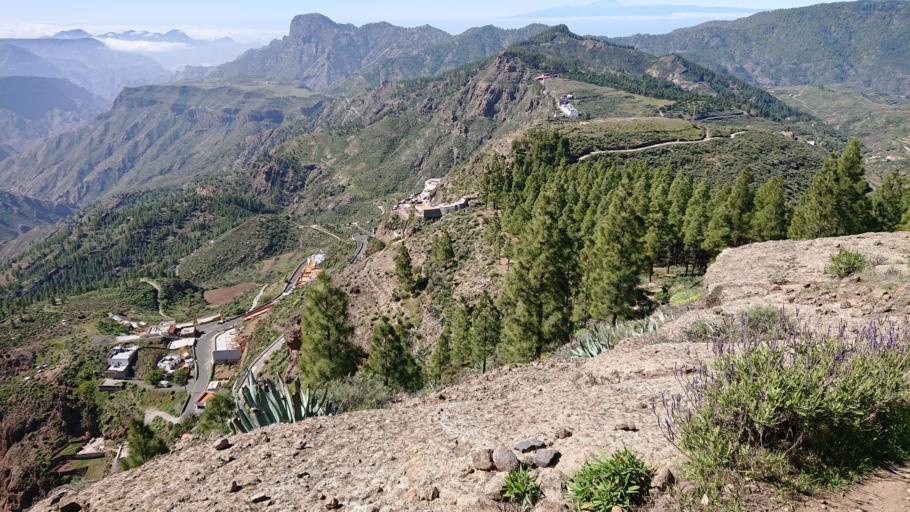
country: ES
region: Canary Islands
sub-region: Provincia de Las Palmas
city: Artenara
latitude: 28.0188
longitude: -15.6396
